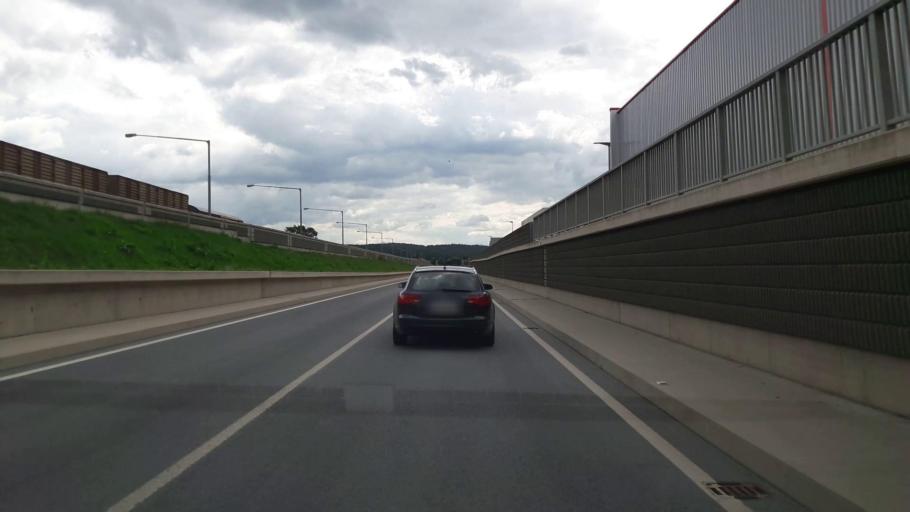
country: AT
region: Styria
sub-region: Politischer Bezirk Weiz
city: Krottendorf
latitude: 47.1988
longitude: 15.6508
